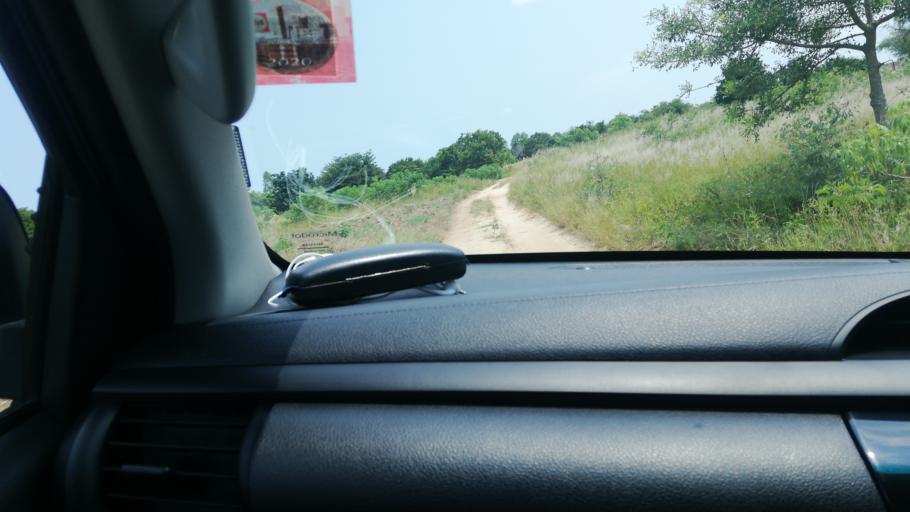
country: MZ
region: Maputo
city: Matola
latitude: -26.1100
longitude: 32.4304
